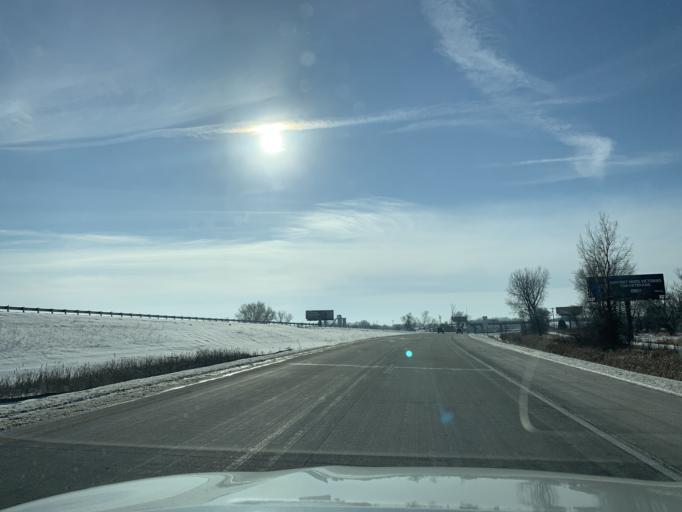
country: US
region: Minnesota
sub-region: Anoka County
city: Columbus
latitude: 45.2181
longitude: -93.0308
